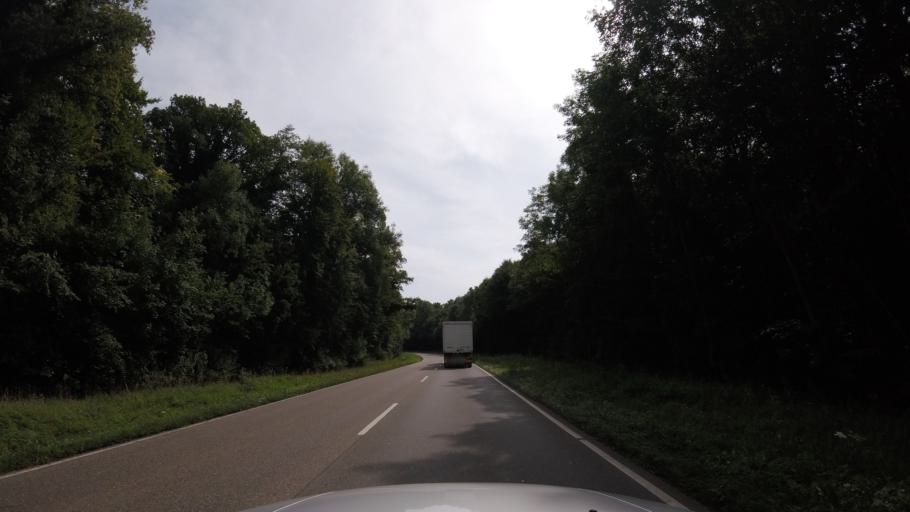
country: DE
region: Baden-Wuerttemberg
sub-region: Regierungsbezirk Stuttgart
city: Grossbottwar
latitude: 48.9878
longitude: 9.3090
